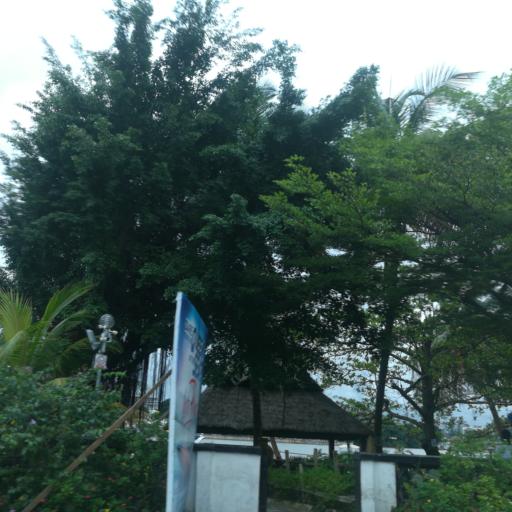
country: NG
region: Lagos
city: Ikoyi
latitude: 6.4477
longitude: 3.4539
